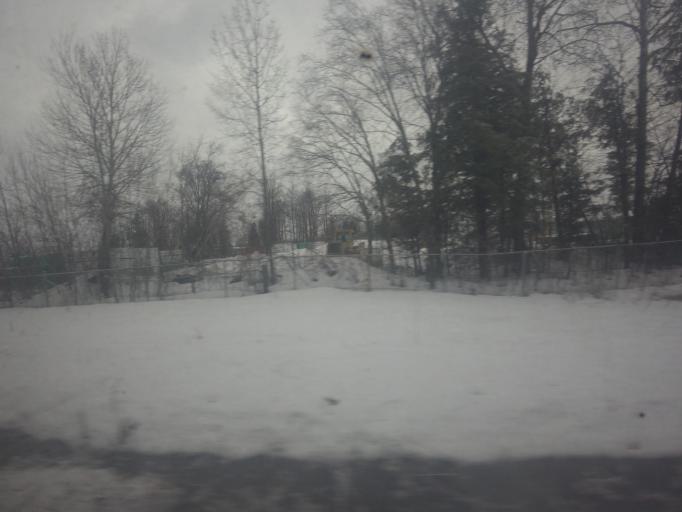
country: CA
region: Ontario
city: Bells Corners
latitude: 45.2462
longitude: -75.7963
